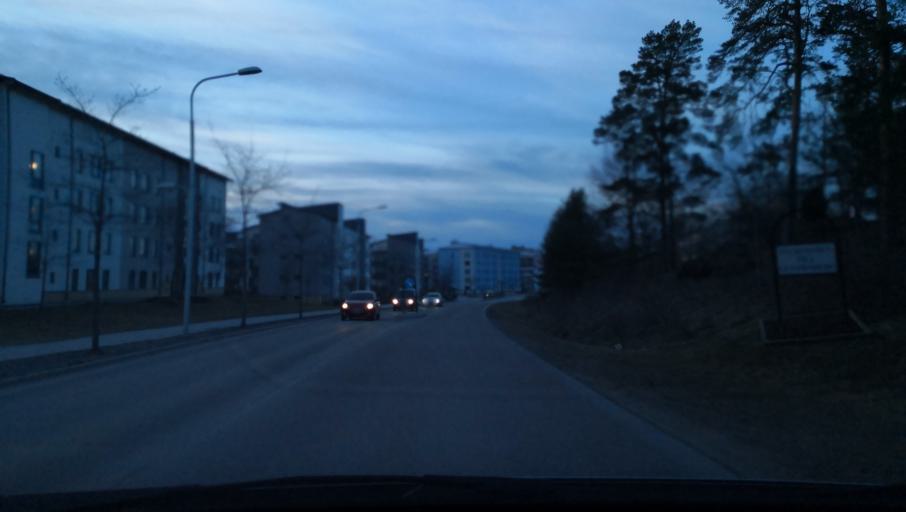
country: SE
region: Stockholm
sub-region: Varmdo Kommun
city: Gustavsberg
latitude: 59.3178
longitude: 18.3897
